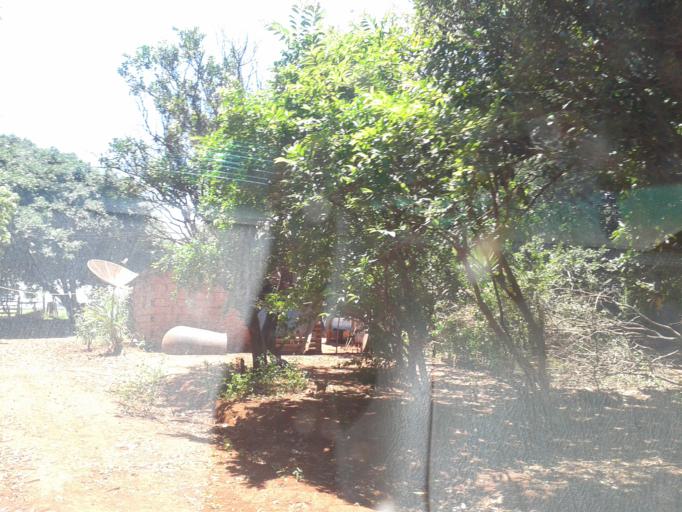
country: BR
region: Minas Gerais
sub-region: Centralina
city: Centralina
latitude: -18.6235
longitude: -49.2770
